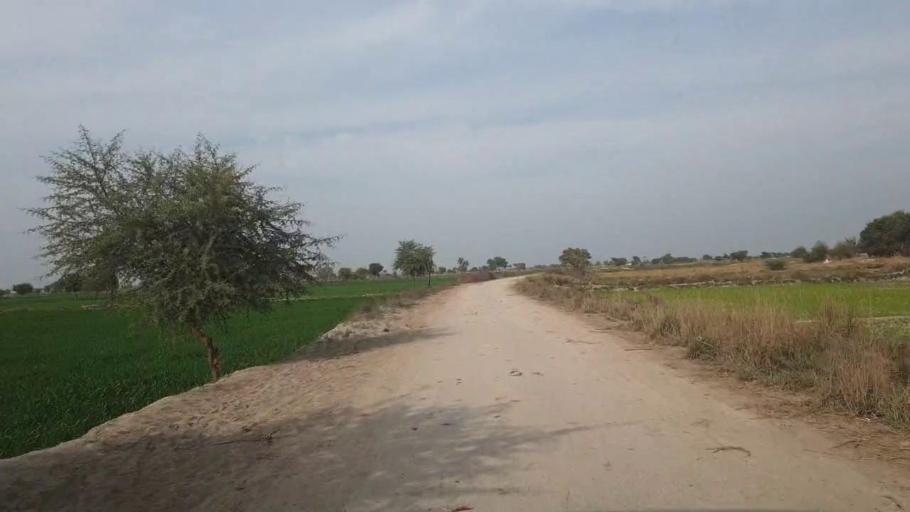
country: PK
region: Sindh
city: Shahpur Chakar
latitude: 26.1110
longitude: 68.5048
